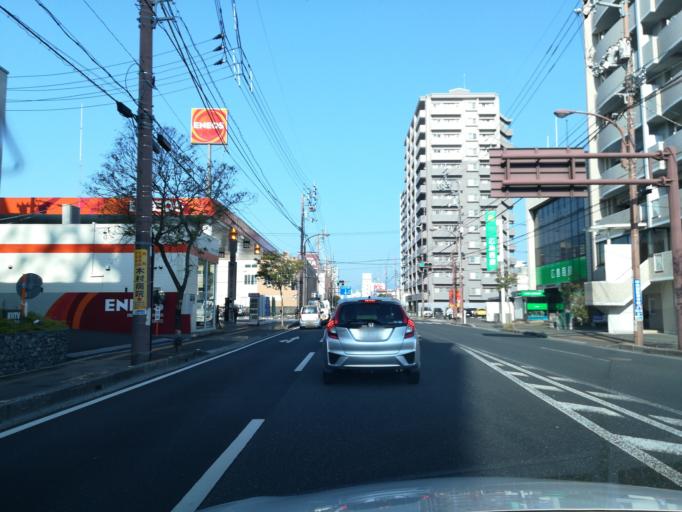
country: JP
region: Kochi
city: Kochi-shi
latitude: 33.5658
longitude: 133.5495
